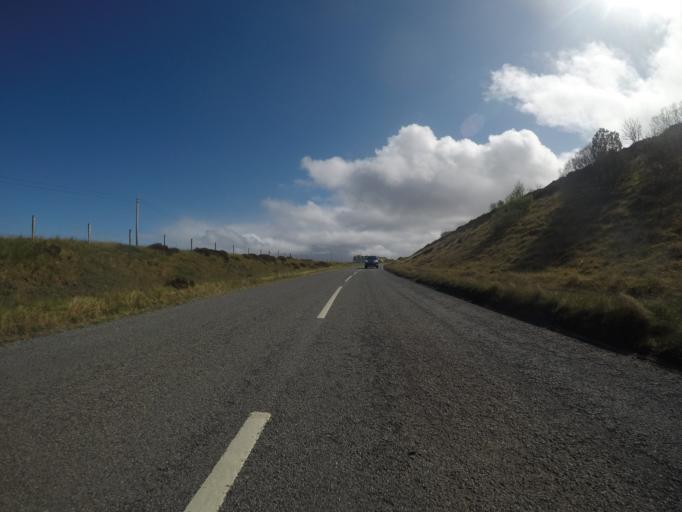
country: GB
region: Scotland
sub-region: Highland
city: Portree
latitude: 57.5763
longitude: -6.1554
